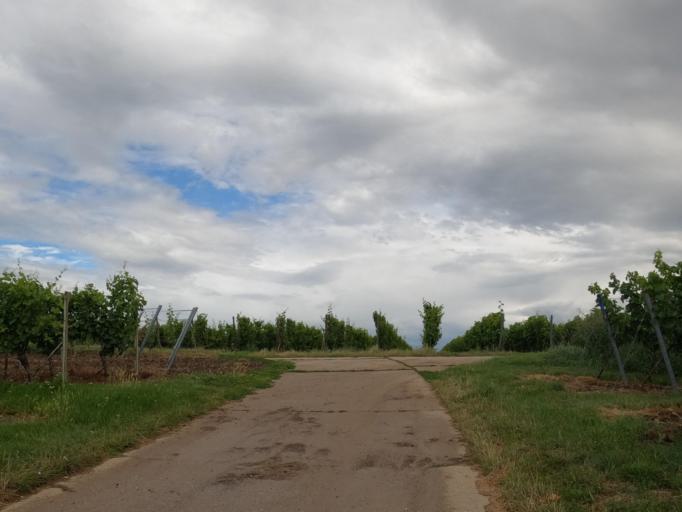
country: DE
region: Rheinland-Pfalz
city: Bissersheim
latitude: 49.5453
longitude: 8.2001
